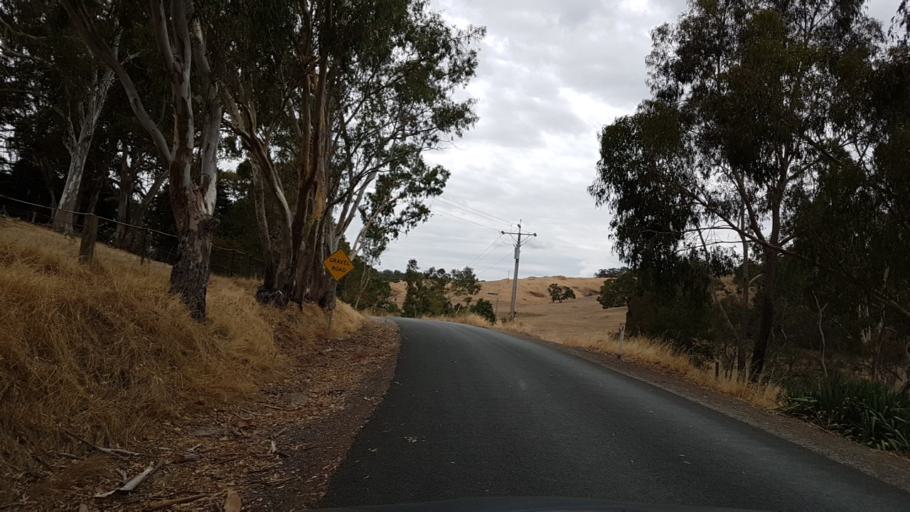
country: AU
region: South Australia
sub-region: Adelaide Hills
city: Gumeracha
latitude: -34.8118
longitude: 138.8100
